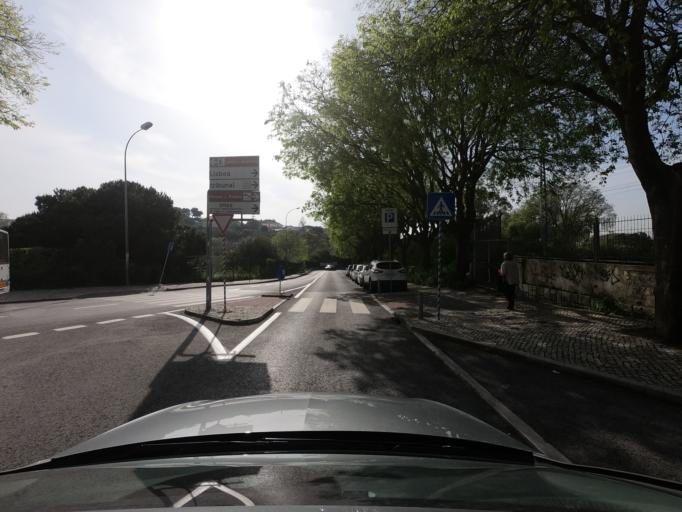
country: PT
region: Lisbon
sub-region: Oeiras
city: Carcavelos
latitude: 38.6883
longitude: -9.3168
